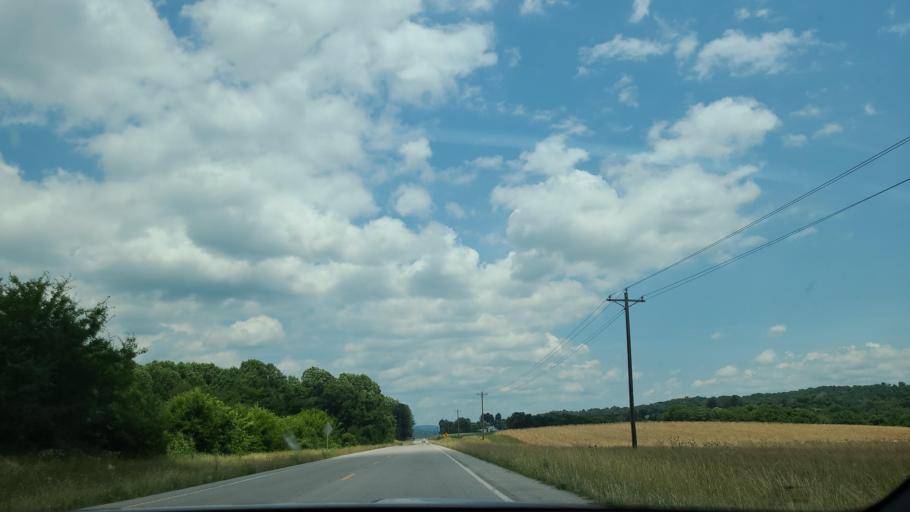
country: US
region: Tennessee
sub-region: Bledsoe County
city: Pikeville
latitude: 35.6246
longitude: -85.1808
